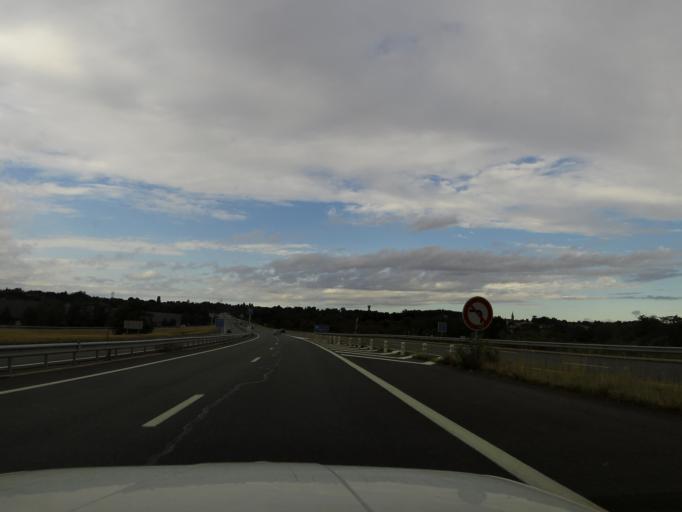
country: FR
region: Rhone-Alpes
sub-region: Departement du Rhone
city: Saint-Laurent-de-Mure
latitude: 45.6896
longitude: 5.0614
